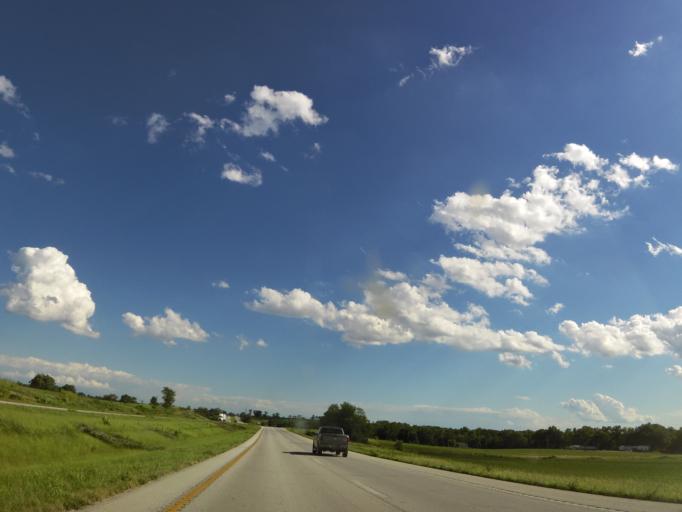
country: US
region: Missouri
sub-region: Marion County
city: Palmyra
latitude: 39.9076
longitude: -91.5255
